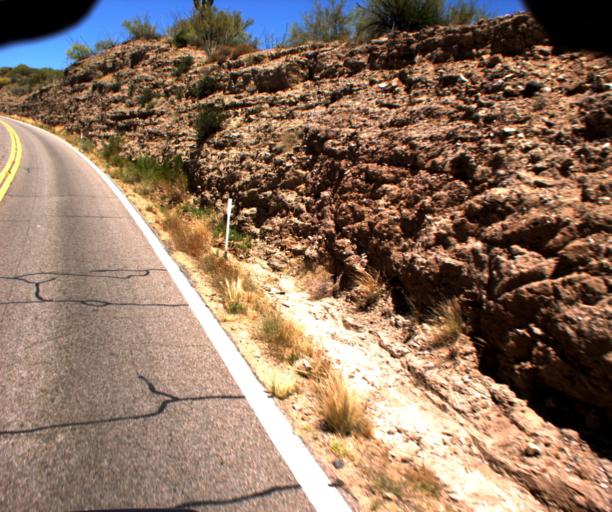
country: US
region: Arizona
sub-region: Pinal County
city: Kearny
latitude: 33.1604
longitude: -110.8044
